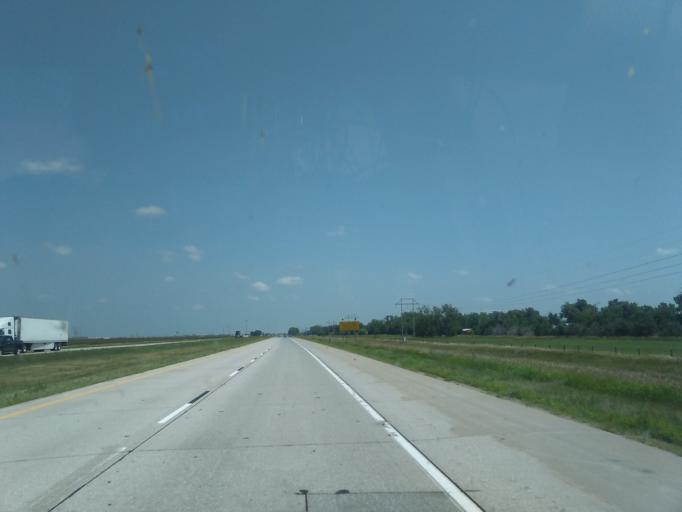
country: US
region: Nebraska
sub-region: Dawson County
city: Lexington
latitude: 40.7487
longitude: -99.7714
